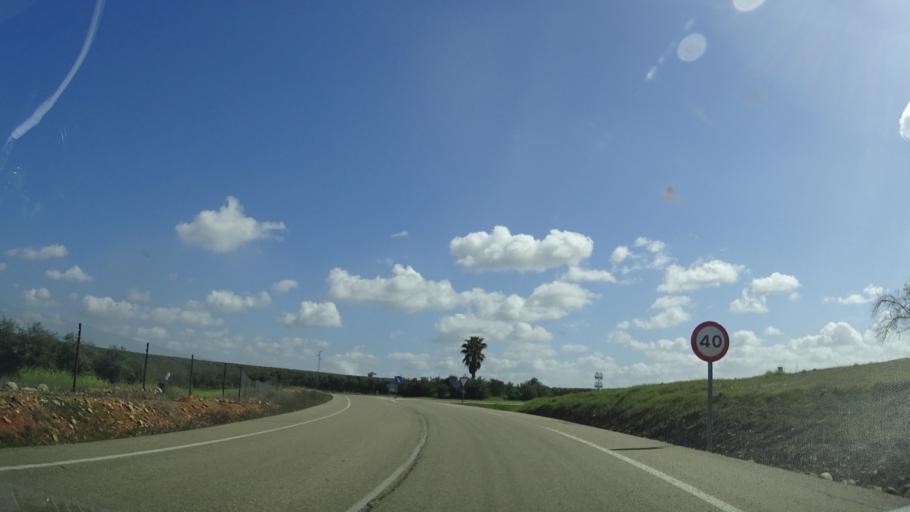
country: ES
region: Andalusia
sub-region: Province of Cordoba
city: Montoro
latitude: 38.0036
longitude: -4.3454
